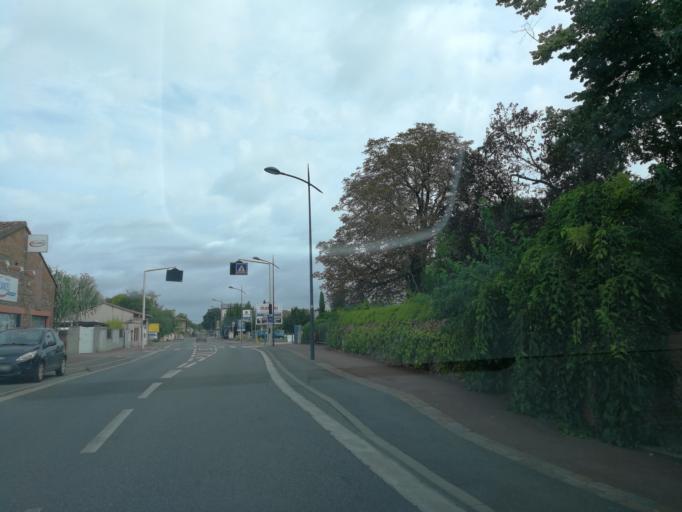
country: FR
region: Midi-Pyrenees
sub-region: Departement de la Haute-Garonne
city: Aucamville
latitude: 43.6543
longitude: 1.4323
